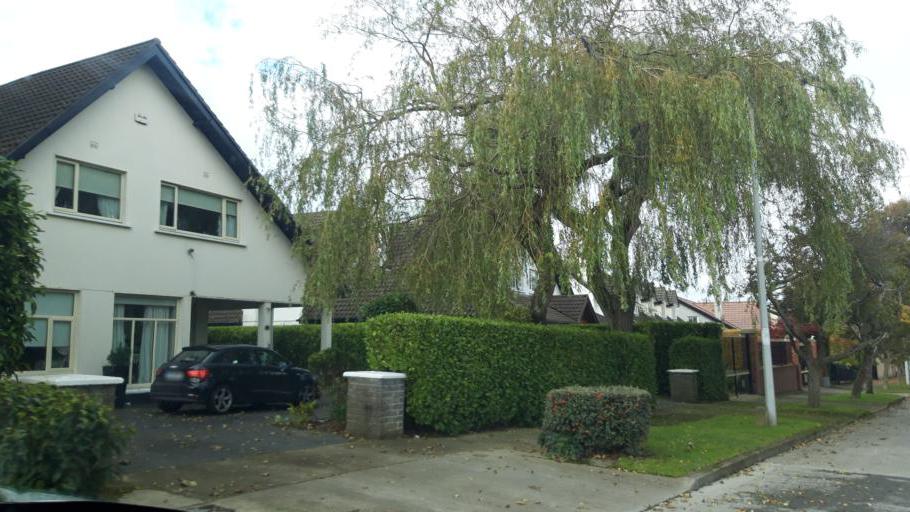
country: IE
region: Leinster
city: Mount Merrion
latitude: 53.2965
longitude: -6.2273
